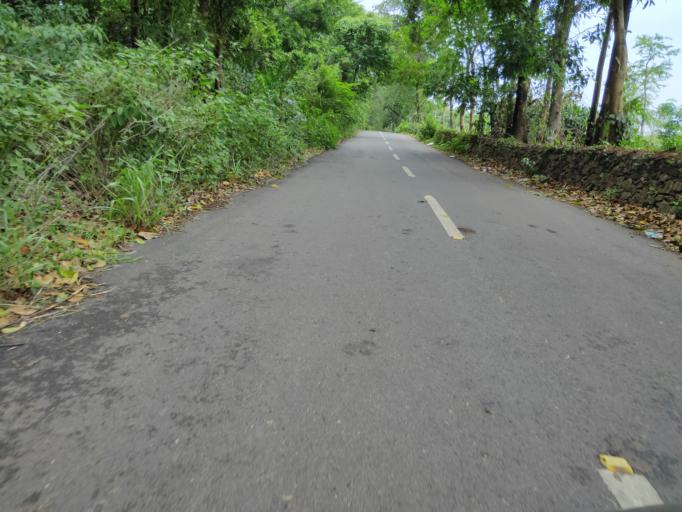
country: IN
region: Kerala
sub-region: Malappuram
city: Manjeri
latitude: 11.2261
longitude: 76.2507
